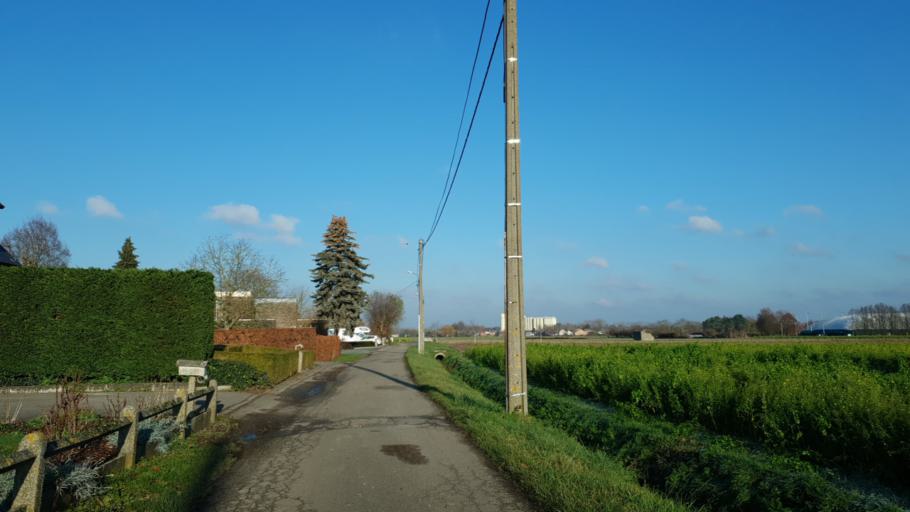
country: BE
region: Flanders
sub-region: Provincie Vlaams-Brabant
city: Herent
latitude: 50.9137
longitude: 4.6743
